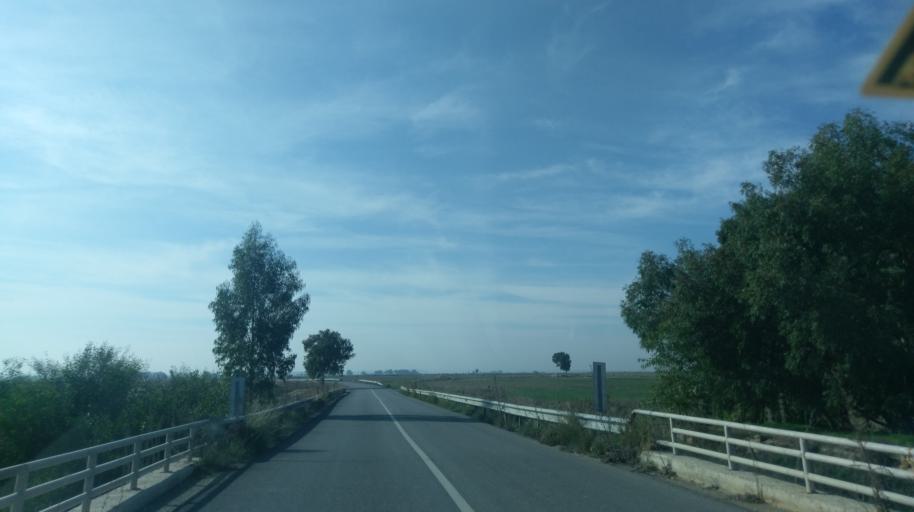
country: CY
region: Larnaka
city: Athienou
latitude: 35.1895
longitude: 33.5975
